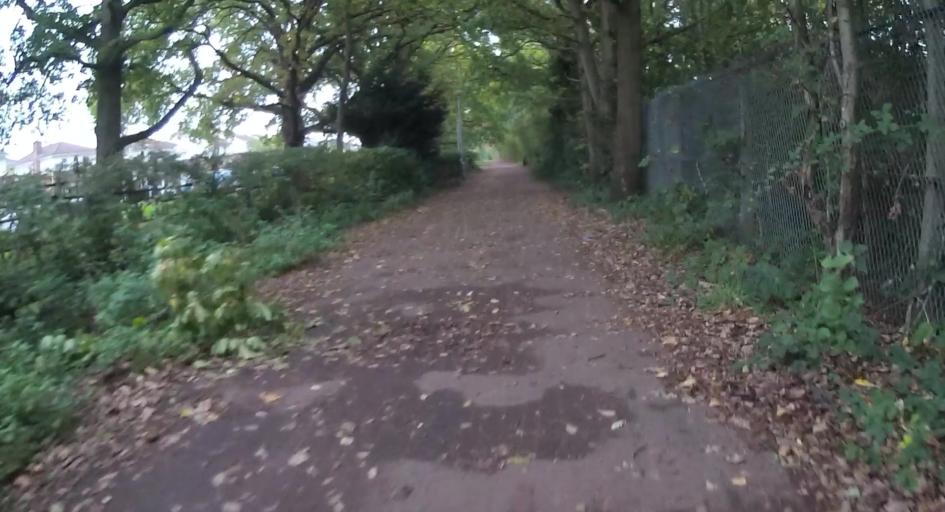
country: GB
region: England
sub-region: Bracknell Forest
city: Crowthorne
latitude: 51.3979
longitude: -0.7813
